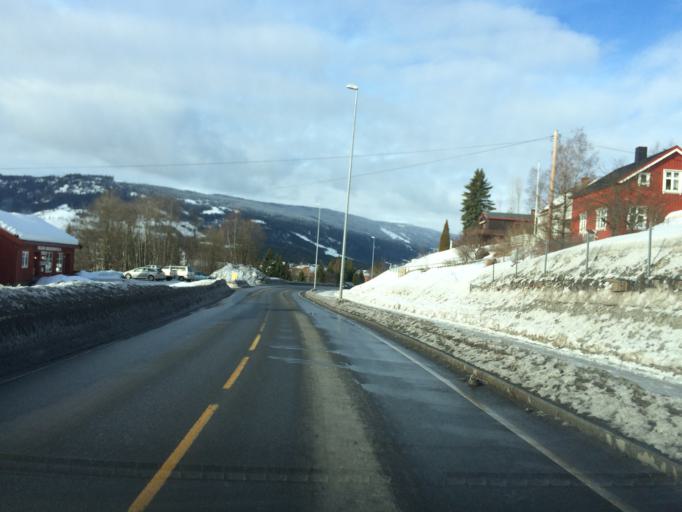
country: NO
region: Oppland
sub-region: Gausdal
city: Segalstad bru
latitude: 61.2252
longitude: 10.2306
